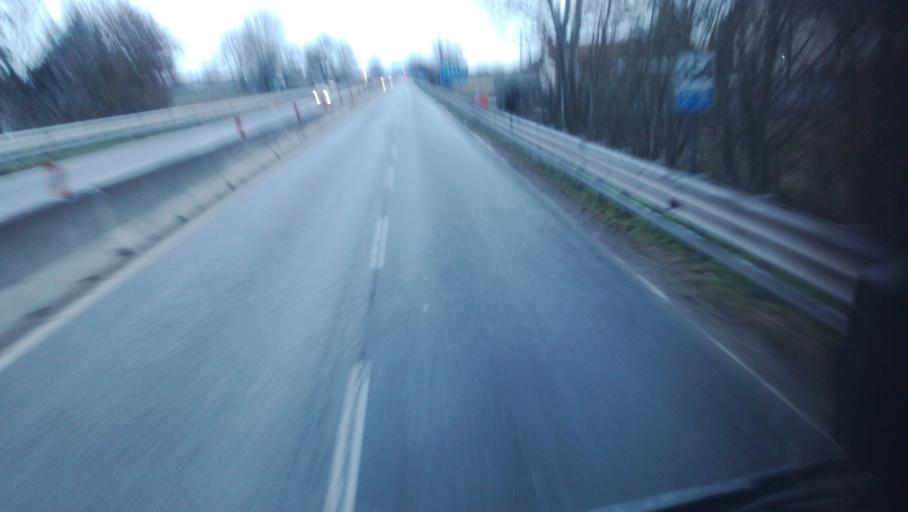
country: IT
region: Emilia-Romagna
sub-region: Provincia di Ravenna
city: Madonna Dell'Albero
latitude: 44.3817
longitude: 12.2027
